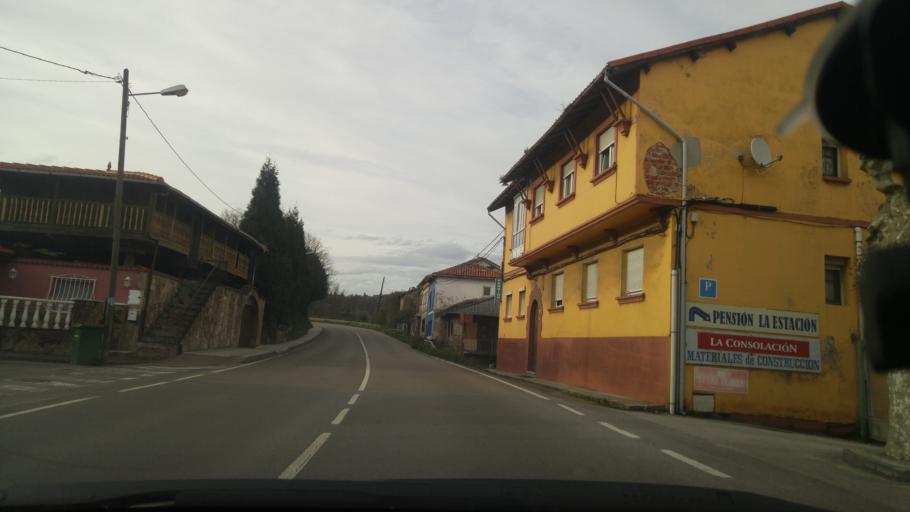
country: ES
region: Asturias
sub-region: Province of Asturias
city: Corvera de Asturias
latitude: 43.5220
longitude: -5.8702
